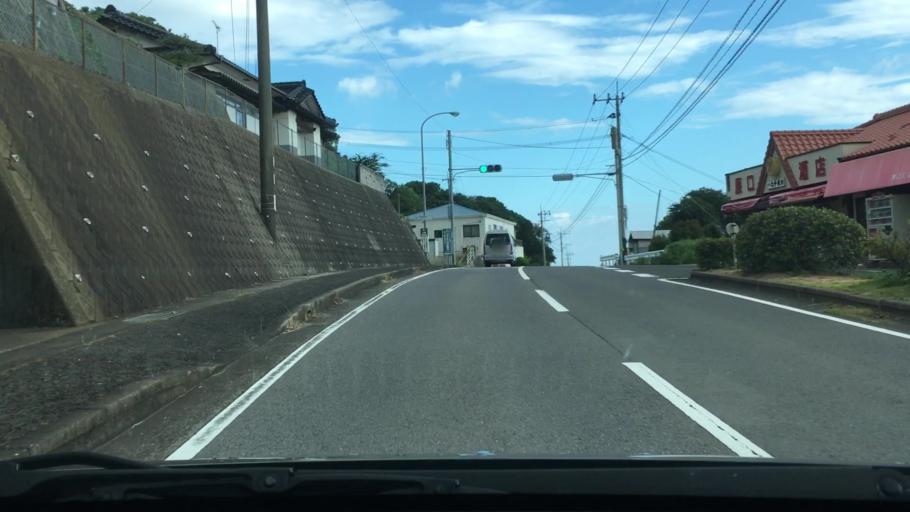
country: JP
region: Nagasaki
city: Togitsu
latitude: 32.8634
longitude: 129.6838
